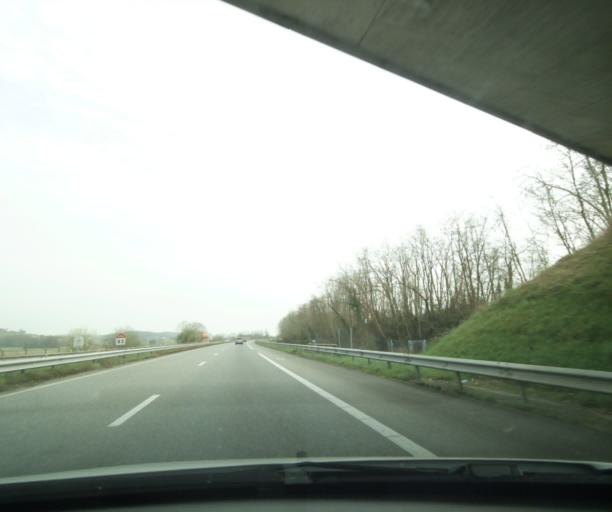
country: FR
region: Aquitaine
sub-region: Departement des Pyrenees-Atlantiques
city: Artix
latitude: 43.4112
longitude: -0.5664
